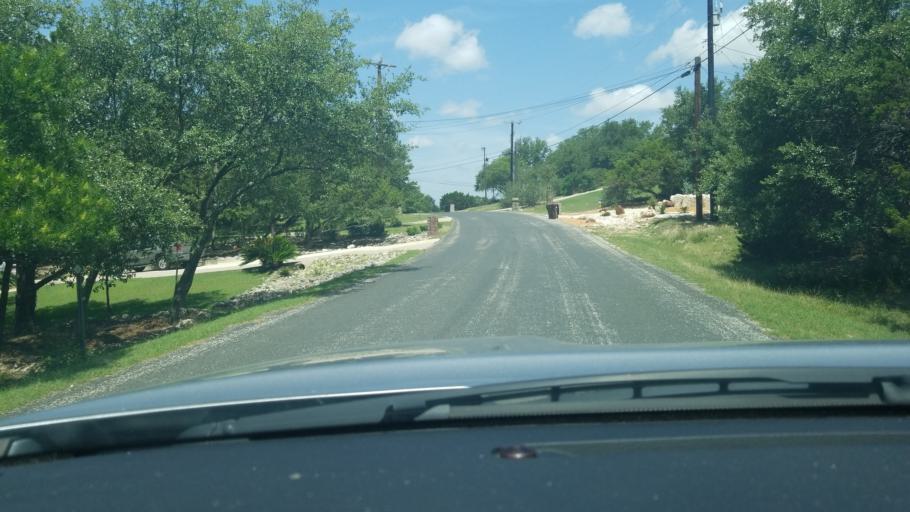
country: US
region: Texas
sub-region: Bexar County
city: Timberwood Park
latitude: 29.6919
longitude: -98.4851
